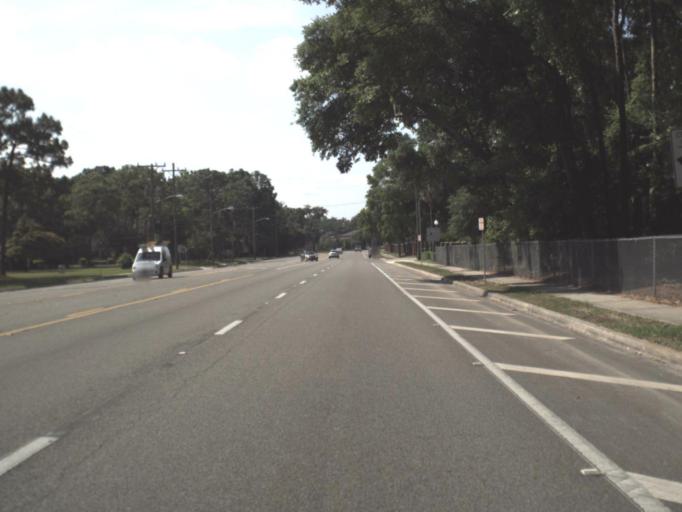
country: US
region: Florida
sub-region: Duval County
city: Jacksonville
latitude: 30.3561
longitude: -81.6041
